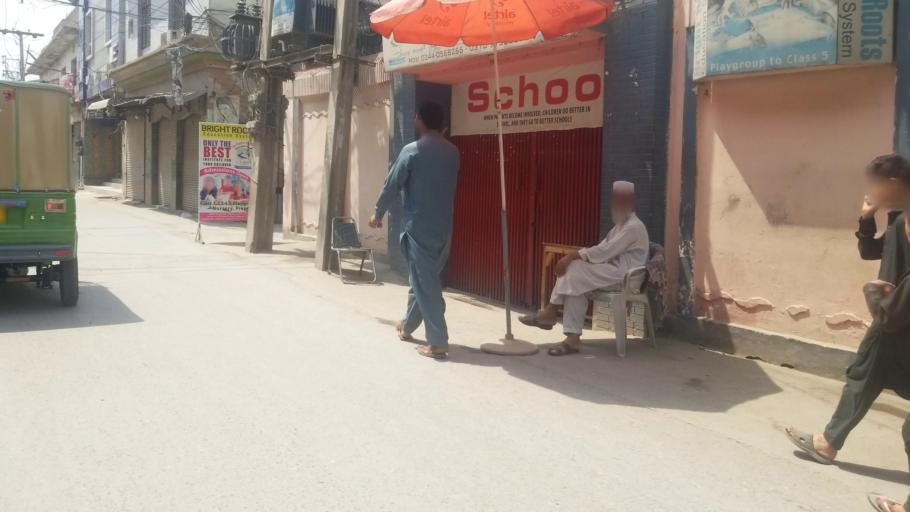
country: PK
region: Khyber Pakhtunkhwa
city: Peshawar
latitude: 34.0298
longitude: 71.5891
